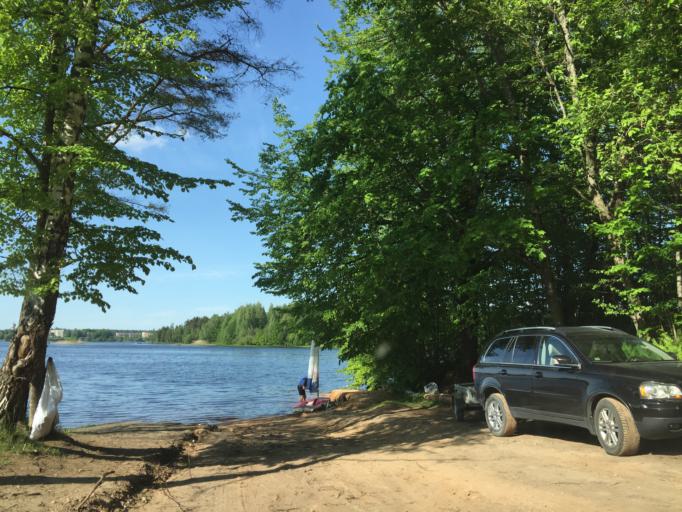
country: LV
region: Ikskile
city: Ikskile
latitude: 56.8299
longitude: 24.4335
